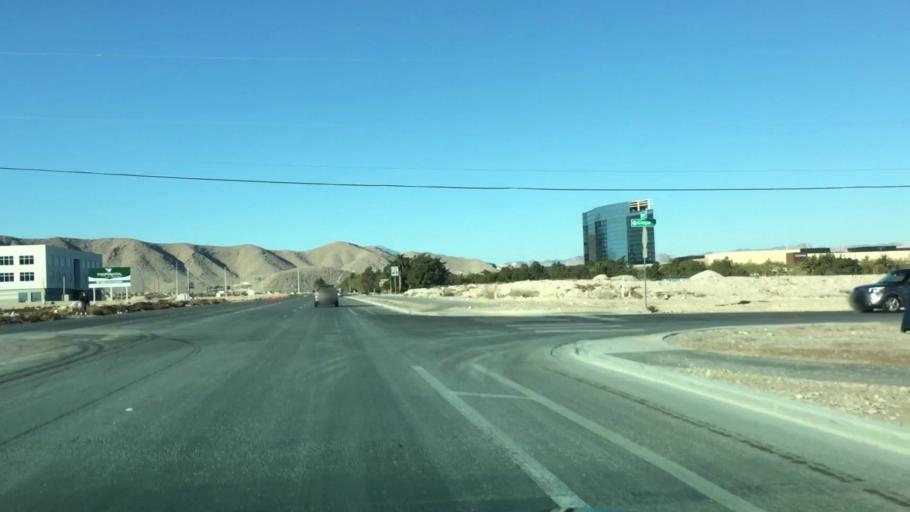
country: US
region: Nevada
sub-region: Clark County
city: Enterprise
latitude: 35.9628
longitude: -115.1633
